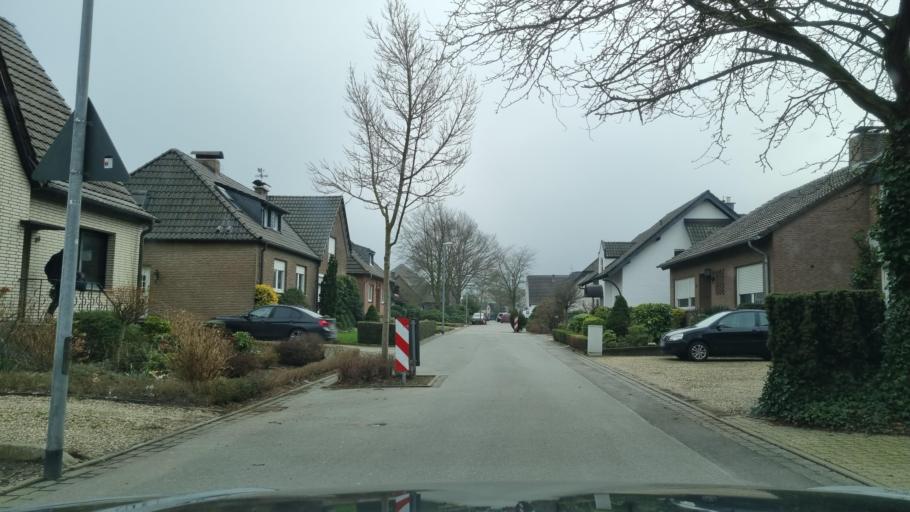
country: DE
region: North Rhine-Westphalia
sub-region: Regierungsbezirk Dusseldorf
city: Kleve
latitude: 51.8112
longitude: 6.1271
